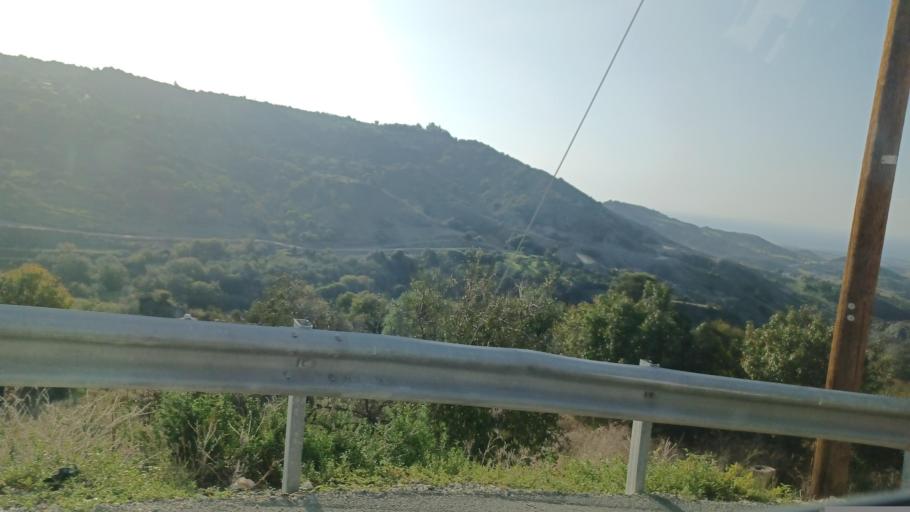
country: CY
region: Pafos
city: Mesogi
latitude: 34.7914
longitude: 32.4917
